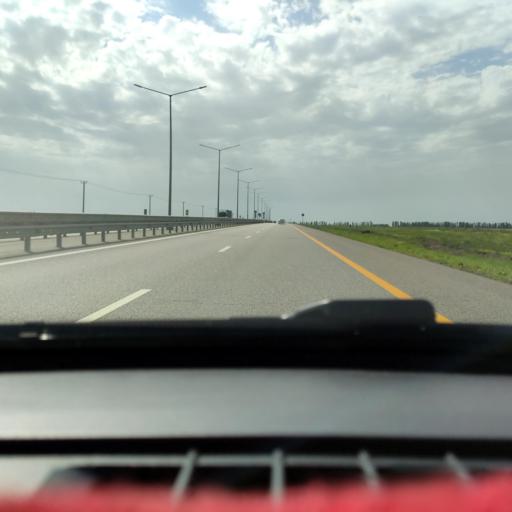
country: RU
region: Voronezj
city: Kashirskoye
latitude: 51.4909
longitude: 39.5306
